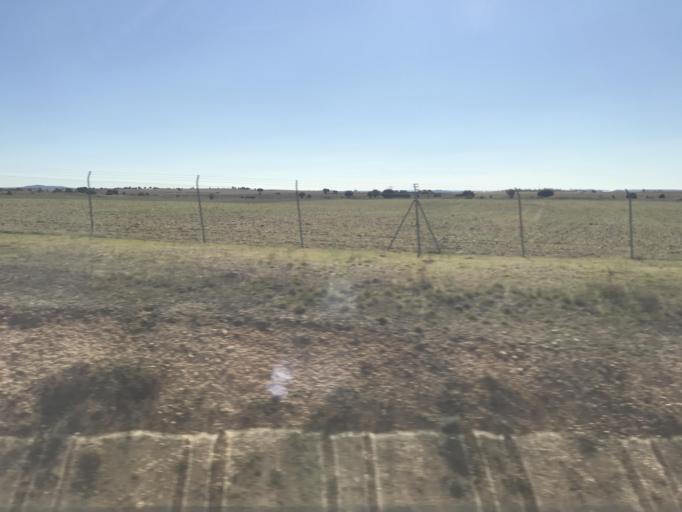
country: ES
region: Castille-La Mancha
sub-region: Provincia de Guadalajara
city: Alaminos
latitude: 40.8861
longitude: -2.7316
